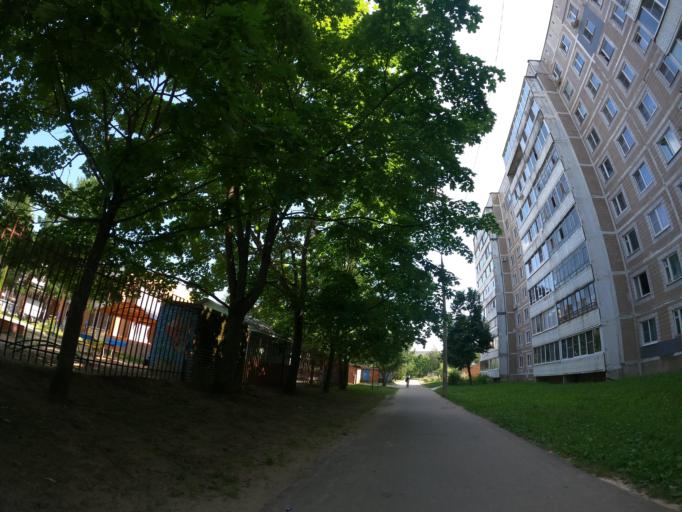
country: RU
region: Kaluga
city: Obninsk
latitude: 55.1173
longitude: 36.5818
